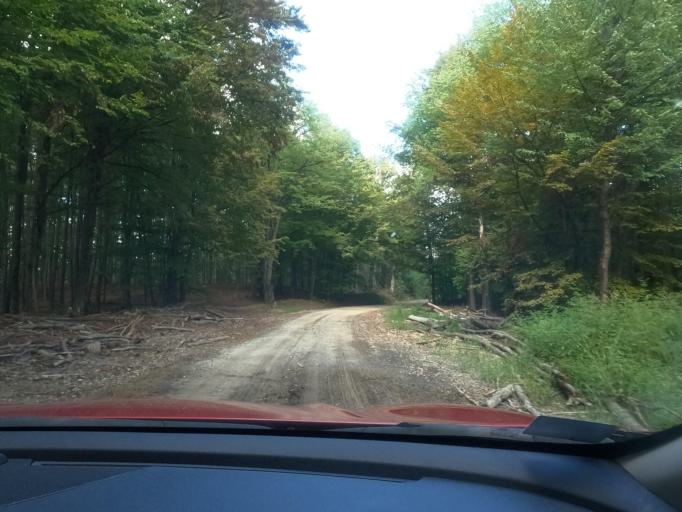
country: BA
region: Federation of Bosnia and Herzegovina
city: Velika Kladusa
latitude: 45.2676
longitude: 15.7782
